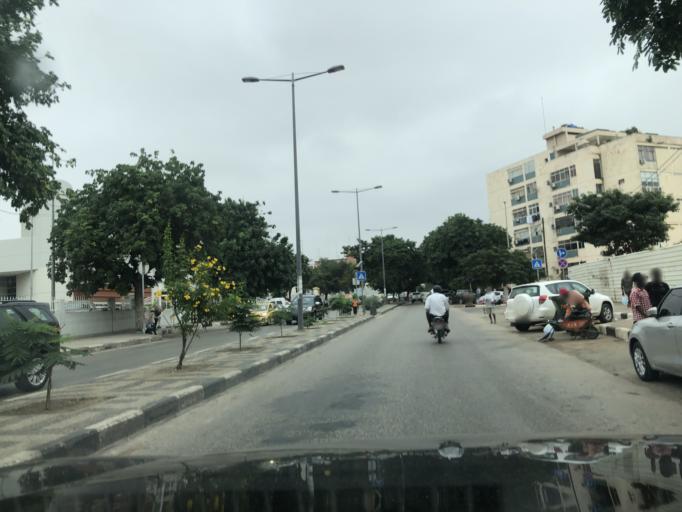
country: AO
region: Luanda
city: Luanda
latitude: -8.8256
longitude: 13.2384
